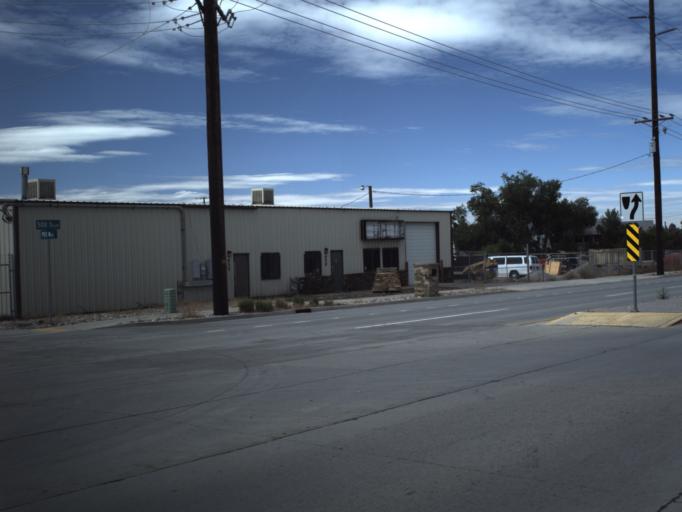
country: US
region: Utah
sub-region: Davis County
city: West Bountiful
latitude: 40.8843
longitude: -111.9062
